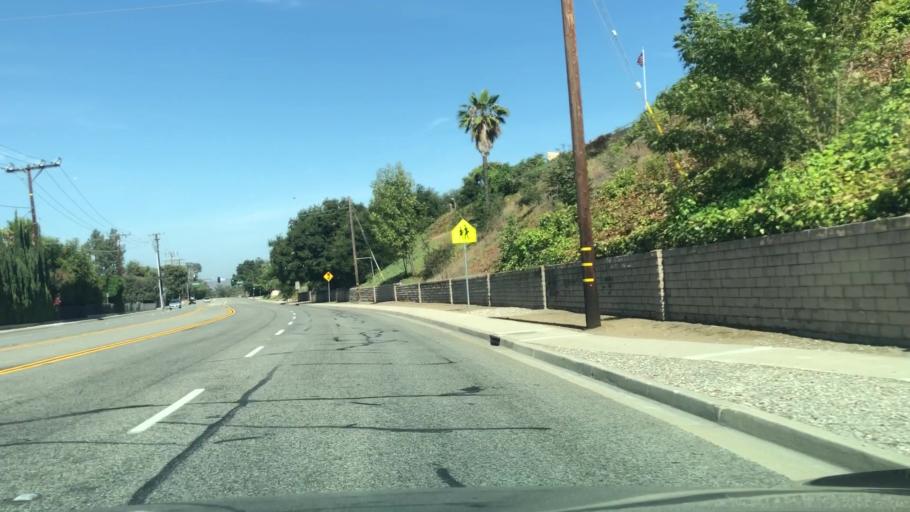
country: US
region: California
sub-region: Ventura County
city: Casa Conejo
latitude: 34.1783
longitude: -118.9404
